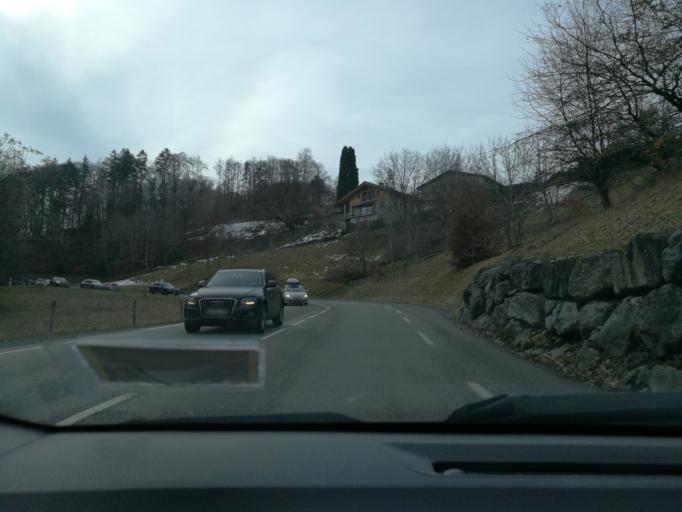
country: FR
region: Rhone-Alpes
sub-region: Departement de la Haute-Savoie
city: Domancy
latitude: 45.9242
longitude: 6.6334
